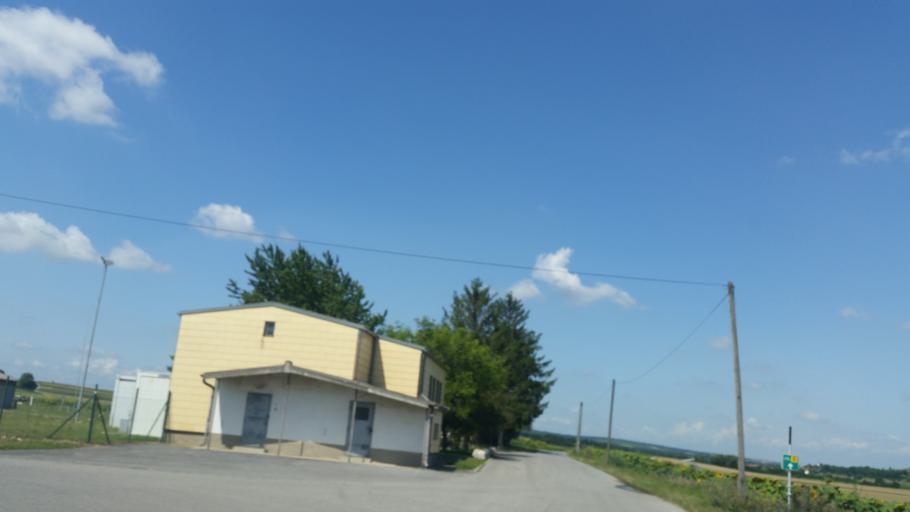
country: AT
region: Lower Austria
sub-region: Politischer Bezirk Ganserndorf
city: Auersthal
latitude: 48.3765
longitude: 16.6756
